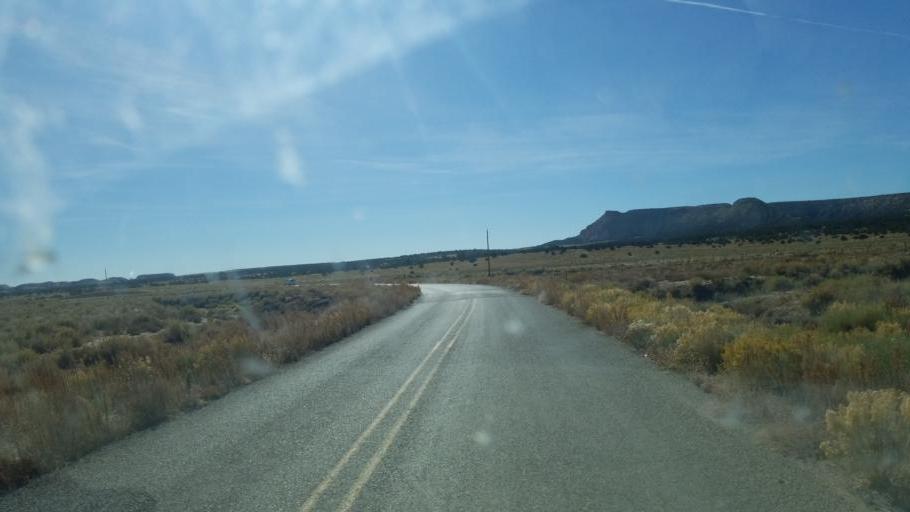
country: US
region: New Mexico
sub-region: McKinley County
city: Thoreau
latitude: 35.4750
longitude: -108.0505
